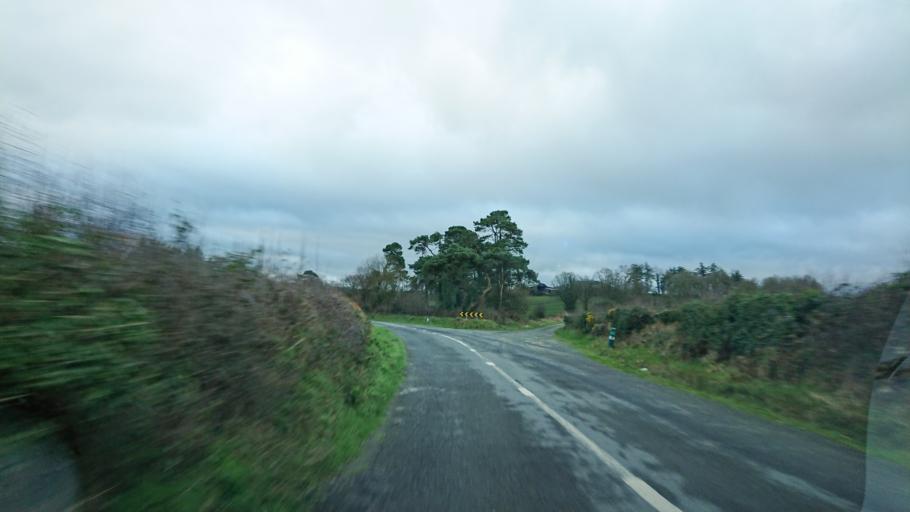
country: IE
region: Munster
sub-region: Waterford
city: Portlaw
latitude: 52.2411
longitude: -7.4160
